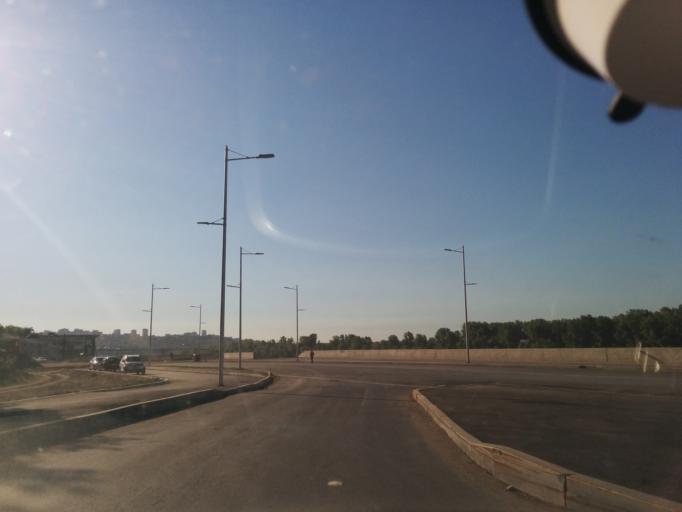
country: RU
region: Bashkortostan
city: Ufa
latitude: 54.7153
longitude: 55.9310
